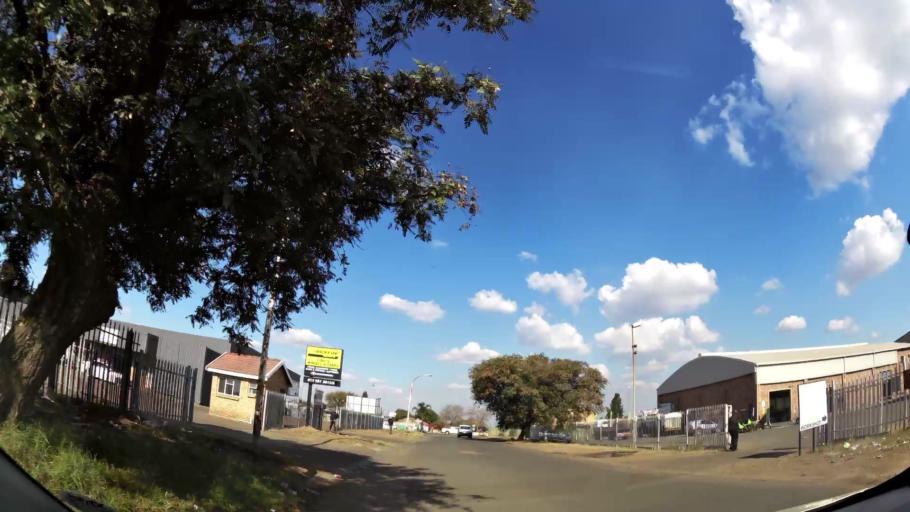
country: ZA
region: Mpumalanga
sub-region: Nkangala District Municipality
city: Witbank
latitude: -25.9029
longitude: 29.2317
